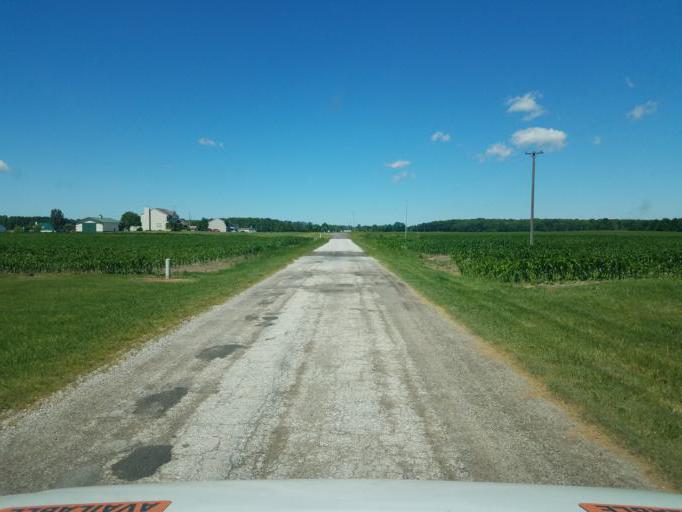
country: US
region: Ohio
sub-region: Morrow County
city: Cardington
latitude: 40.5432
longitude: -82.9418
